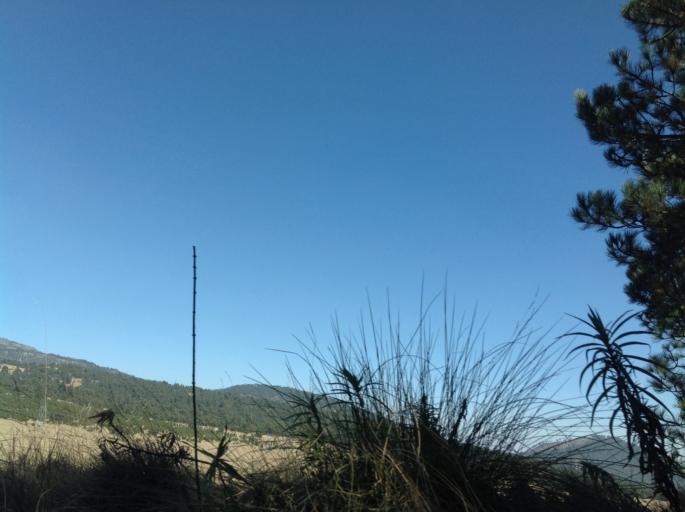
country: MX
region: Mexico
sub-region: Amecameca
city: San Diego Huehuecalco
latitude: 19.0913
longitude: -98.6477
